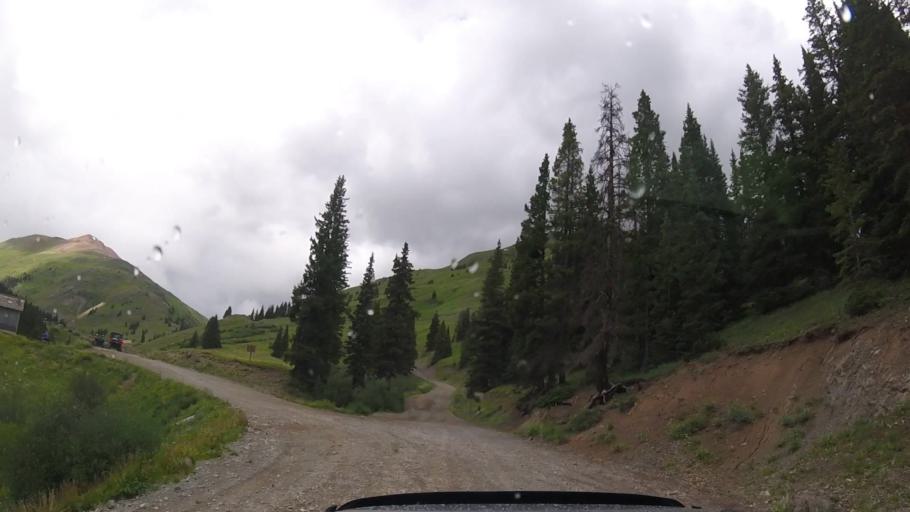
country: US
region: Colorado
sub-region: Ouray County
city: Ouray
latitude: 37.9265
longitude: -107.5631
